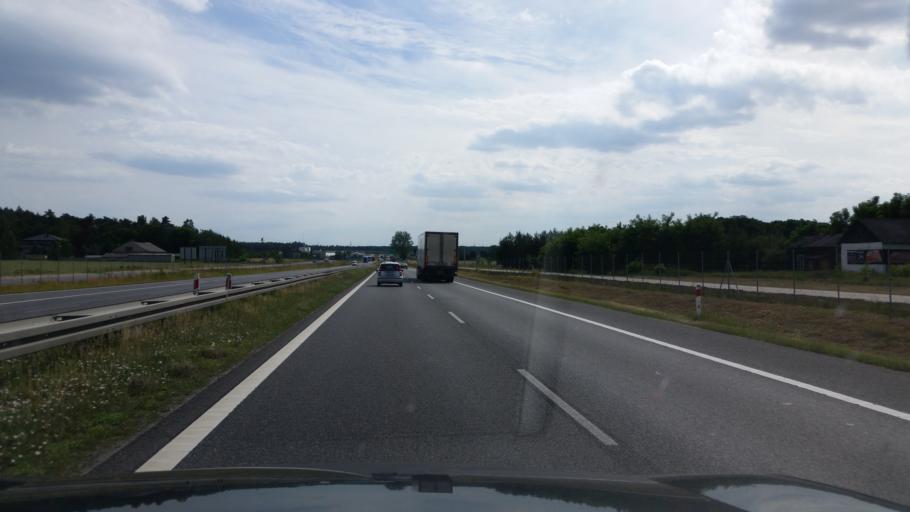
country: PL
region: Masovian Voivodeship
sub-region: Powiat zyrardowski
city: Mszczonow
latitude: 51.9490
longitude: 20.4887
